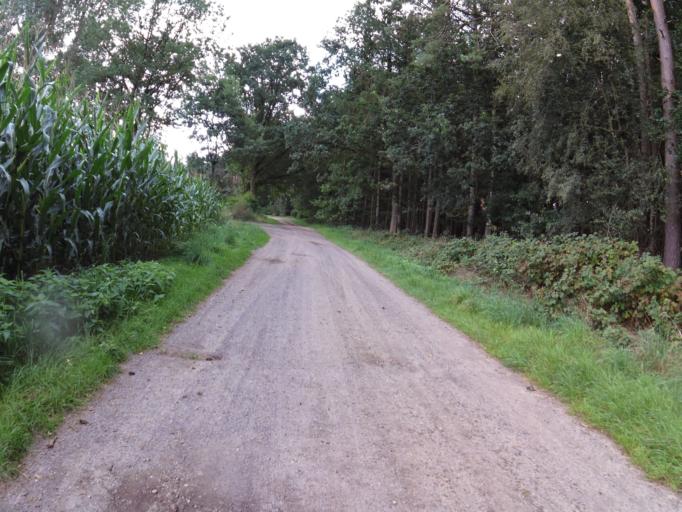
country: DE
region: Lower Saxony
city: Sandbostel
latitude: 53.3794
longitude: 9.1444
